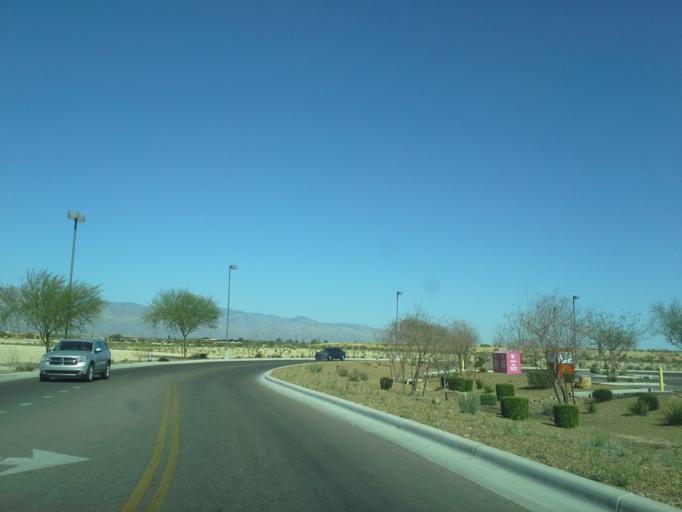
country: US
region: Arizona
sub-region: Pima County
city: South Tucson
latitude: 32.1872
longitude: -110.9537
